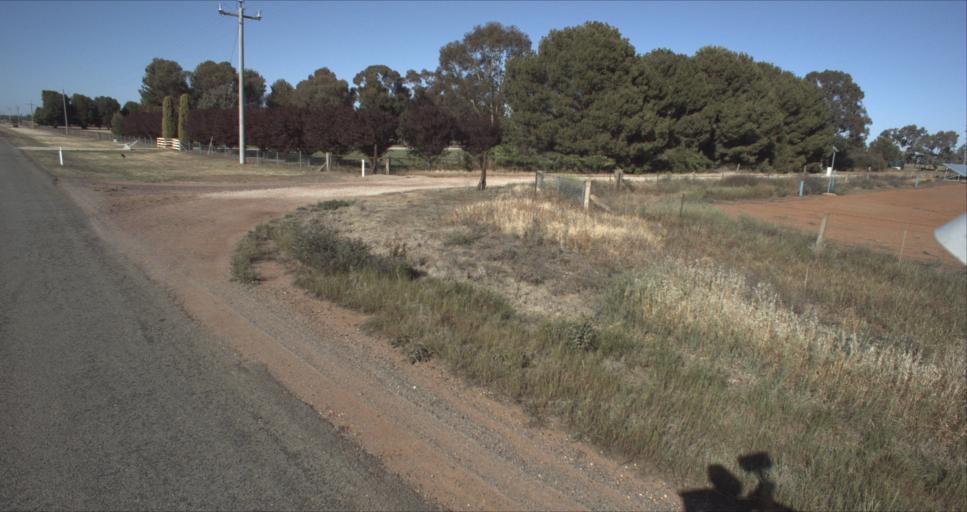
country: AU
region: New South Wales
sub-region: Leeton
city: Leeton
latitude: -34.5840
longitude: 146.2610
